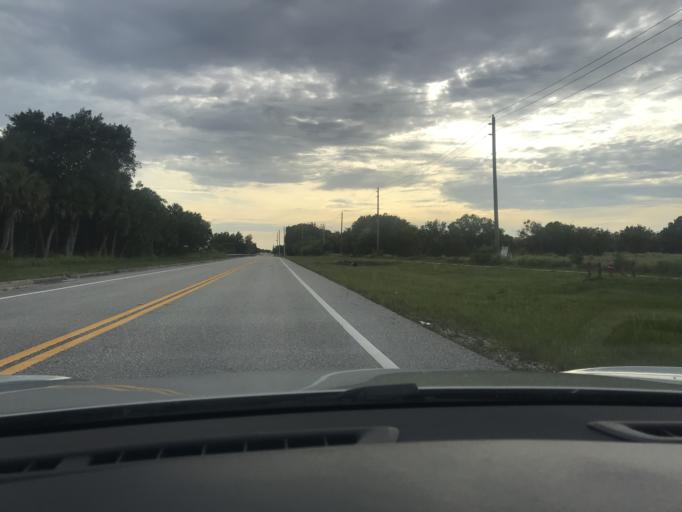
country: US
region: Florida
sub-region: Indian River County
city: West Vero Corridor
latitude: 27.6317
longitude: -80.4659
